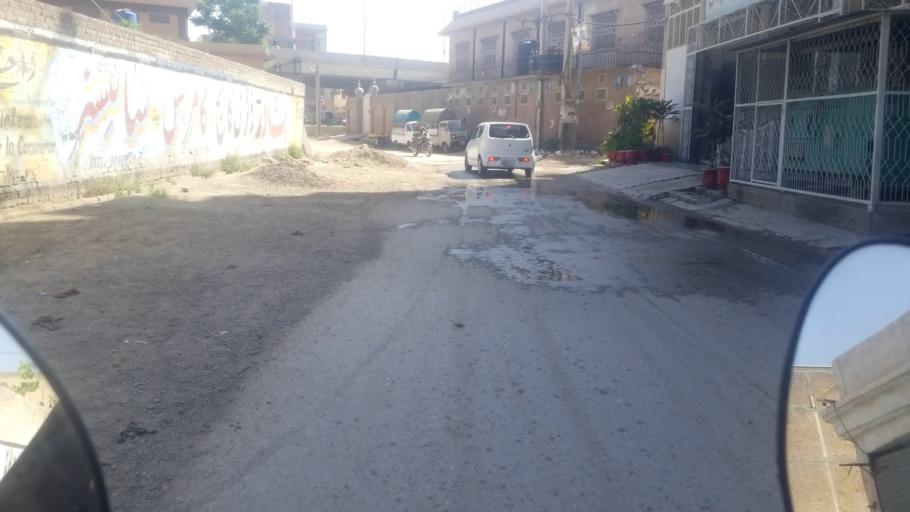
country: PK
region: Khyber Pakhtunkhwa
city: Peshawar
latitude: 34.0162
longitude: 71.5858
